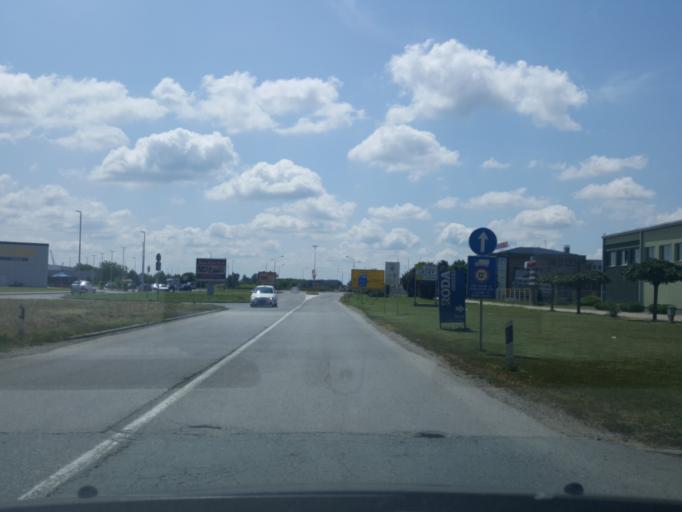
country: RS
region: Autonomna Pokrajina Vojvodina
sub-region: Sremski Okrug
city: Sremska Mitrovica
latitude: 44.9725
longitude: 19.6373
